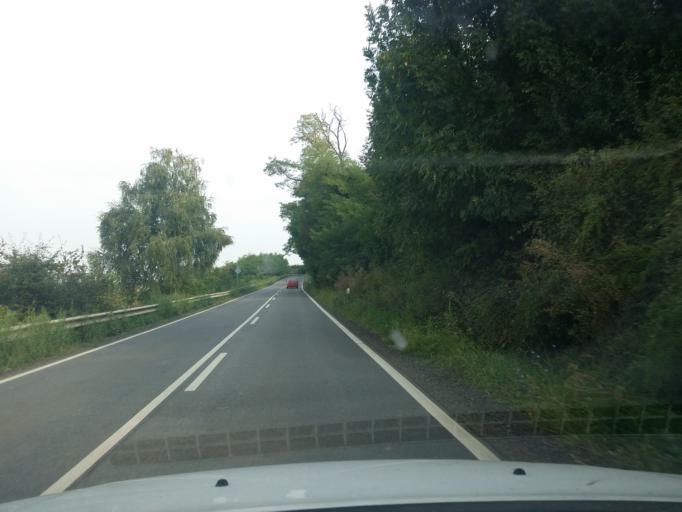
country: HU
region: Pest
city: Acsa
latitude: 47.7655
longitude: 19.3704
